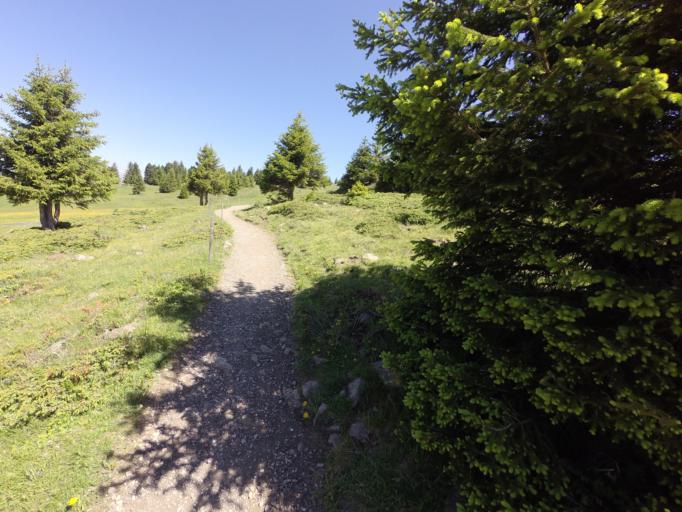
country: IT
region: Trentino-Alto Adige
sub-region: Bolzano
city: Castelrotto
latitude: 46.5600
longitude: 11.6074
